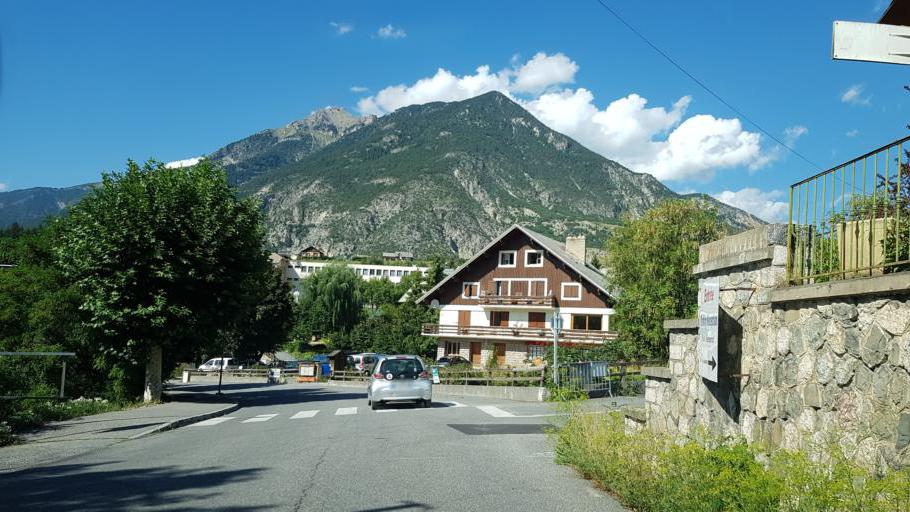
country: FR
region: Provence-Alpes-Cote d'Azur
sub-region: Departement des Hautes-Alpes
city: Guillestre
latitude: 44.6602
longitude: 6.6534
